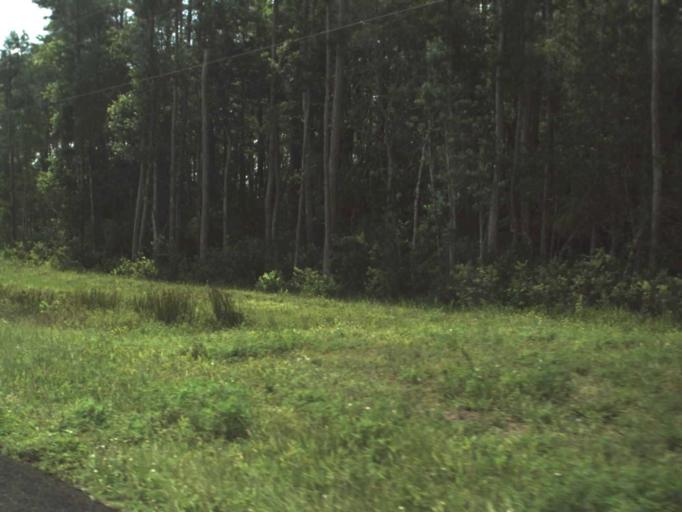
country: US
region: Florida
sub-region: Volusia County
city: Glencoe
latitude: 29.0125
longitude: -80.9981
